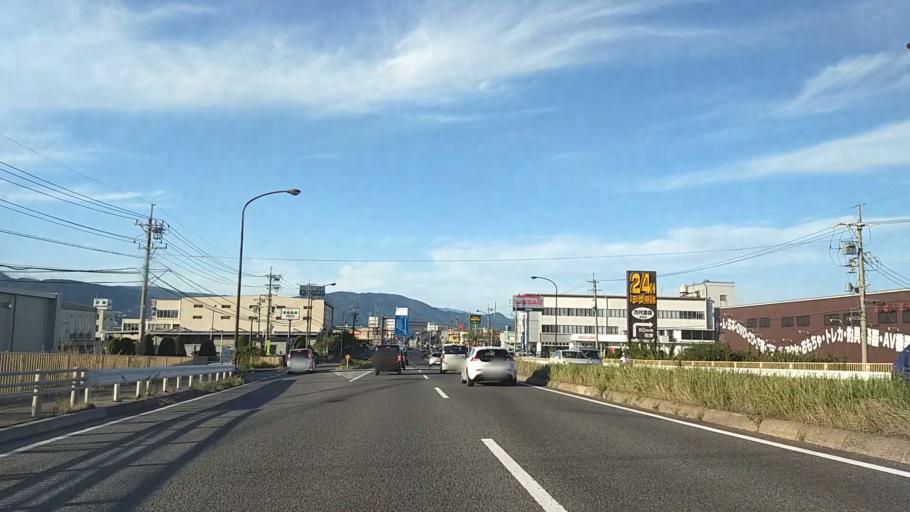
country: JP
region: Nagano
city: Nagano-shi
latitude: 36.6230
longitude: 138.1998
